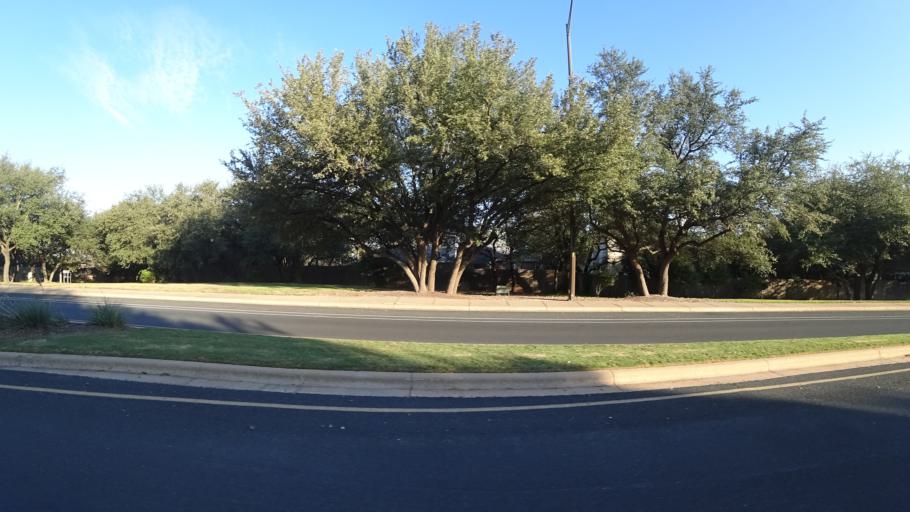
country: US
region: Texas
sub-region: Travis County
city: Hudson Bend
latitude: 30.3769
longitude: -97.8912
